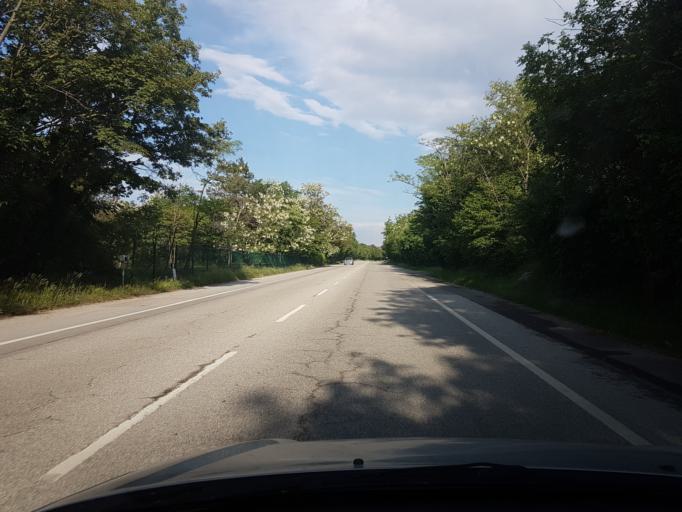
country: IT
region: Friuli Venezia Giulia
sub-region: Provincia di Trieste
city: Villa Opicina
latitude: 45.6812
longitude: 13.7979
